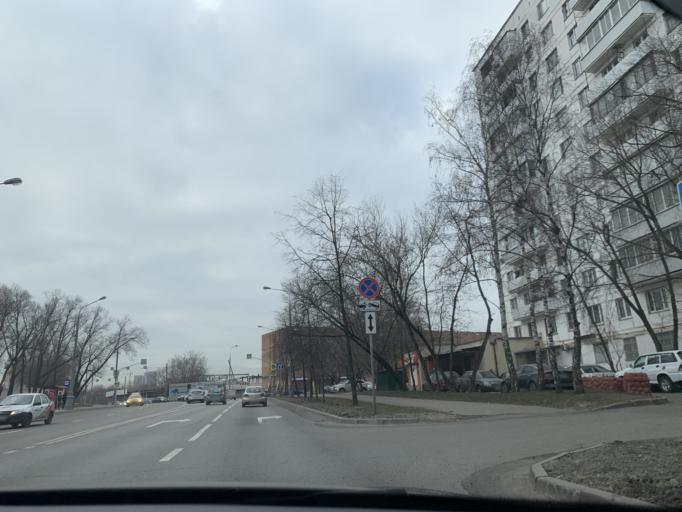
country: RU
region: Moscow
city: Likhobory
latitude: 55.8559
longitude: 37.5667
